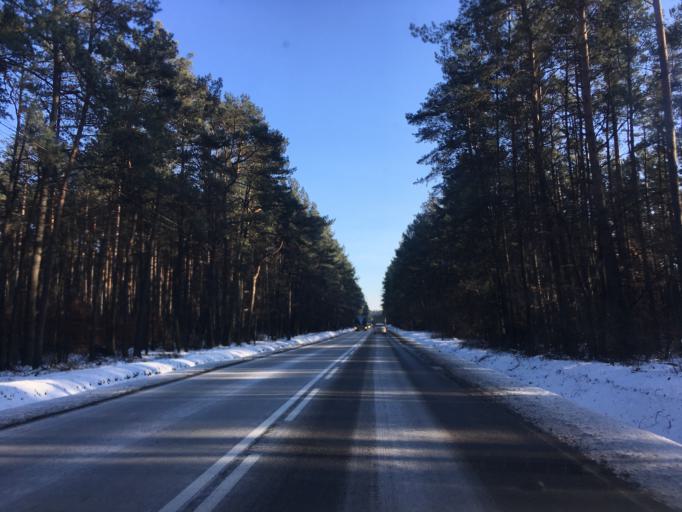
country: PL
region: Pomeranian Voivodeship
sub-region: Powiat koscierski
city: Lipusz
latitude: 54.1241
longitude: 17.8801
